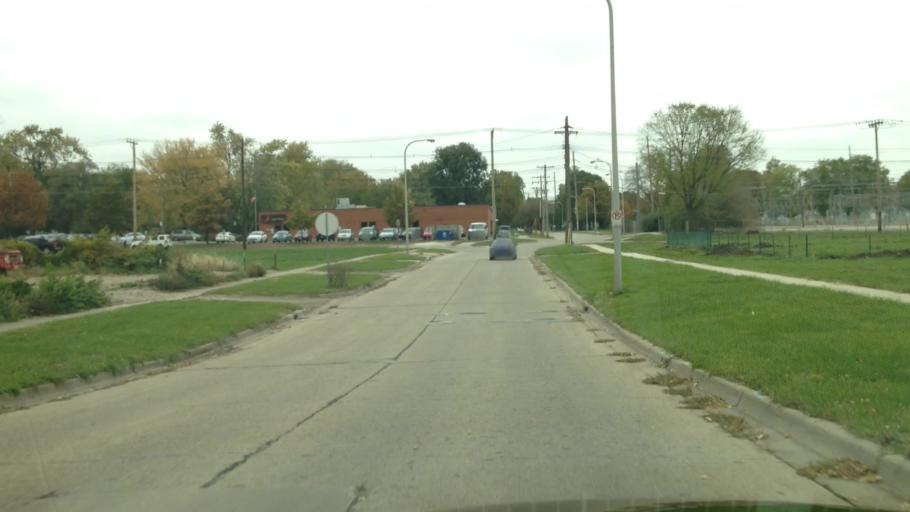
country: US
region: Illinois
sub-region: Champaign County
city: Champaign
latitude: 40.1226
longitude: -88.2412
